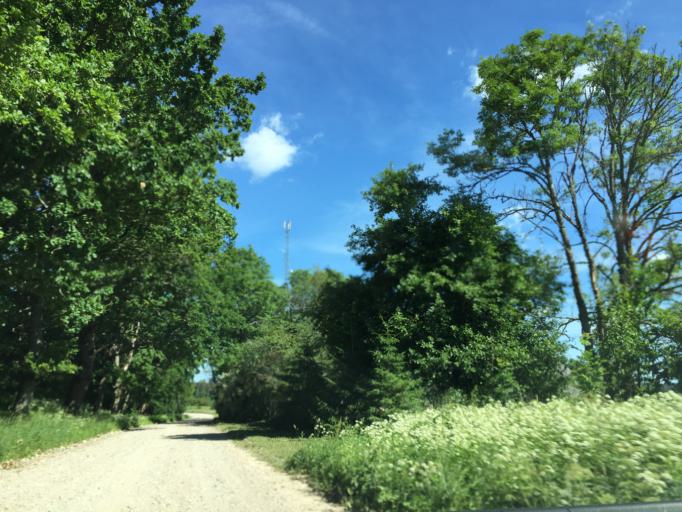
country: LV
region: Dundaga
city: Dundaga
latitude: 57.3585
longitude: 22.0310
